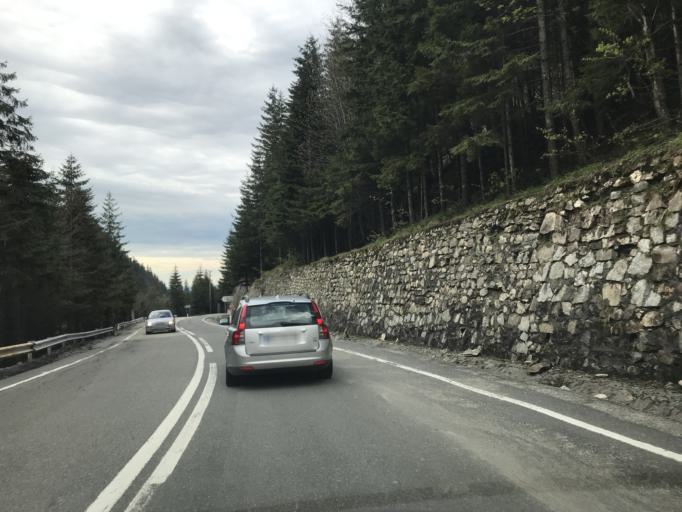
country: RO
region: Sibiu
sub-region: Comuna Cartisoara
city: Cartisoara
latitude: 45.6375
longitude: 24.6064
